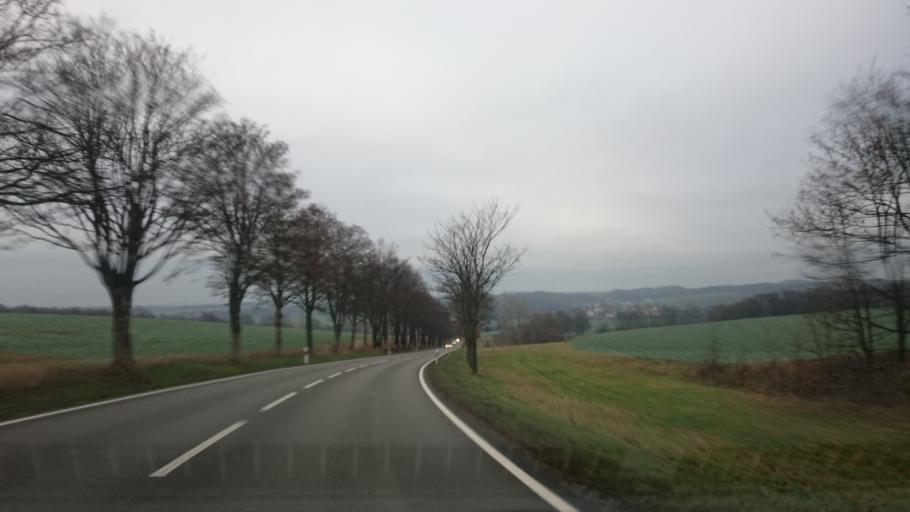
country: DE
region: Saxony
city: Mulsen
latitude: 50.7310
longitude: 12.5597
